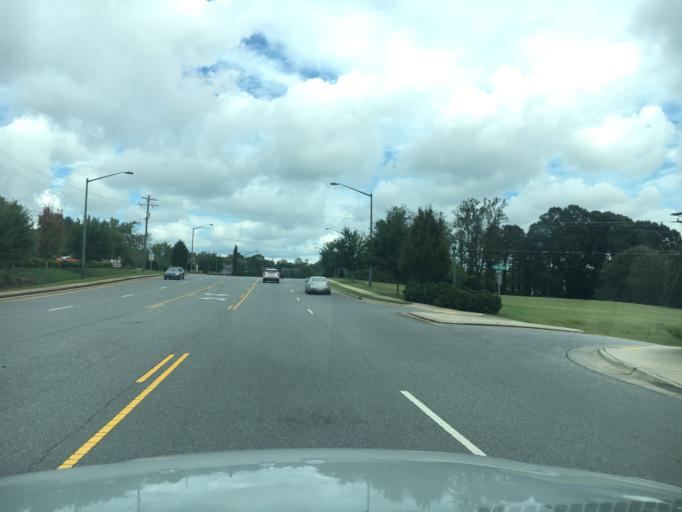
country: US
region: North Carolina
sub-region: Catawba County
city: Hickory
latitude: 35.7316
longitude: -81.3256
